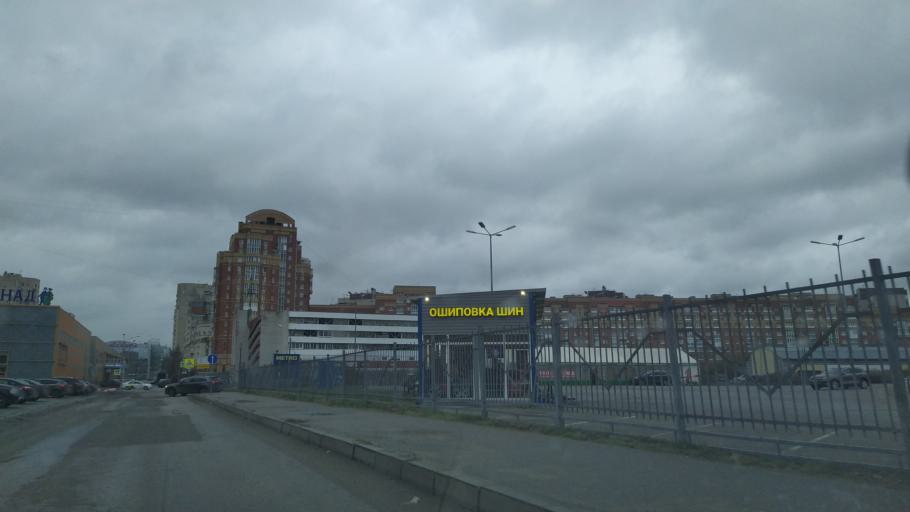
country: RU
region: St.-Petersburg
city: Komendantsky aerodrom
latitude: 60.0027
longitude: 30.2661
